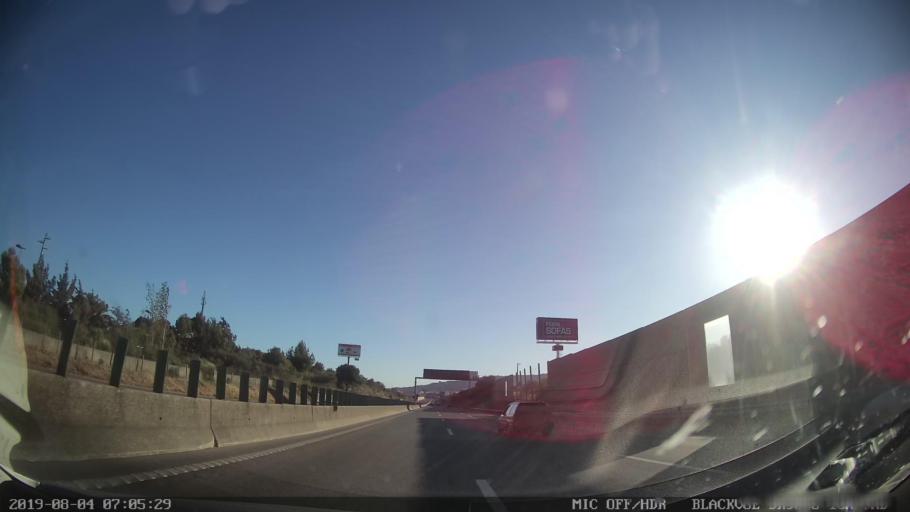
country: PT
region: Lisbon
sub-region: Vila Franca de Xira
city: Sobralinho
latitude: 38.9106
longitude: -9.0313
